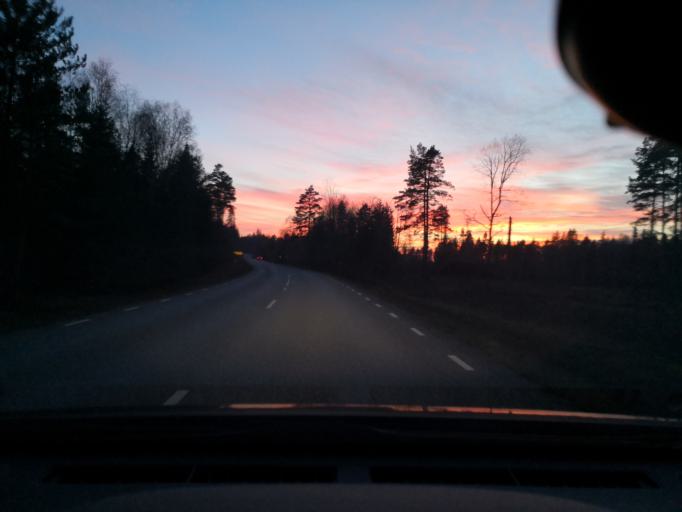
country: SE
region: OErebro
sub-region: Lindesbergs Kommun
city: Frovi
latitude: 59.3934
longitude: 15.4461
